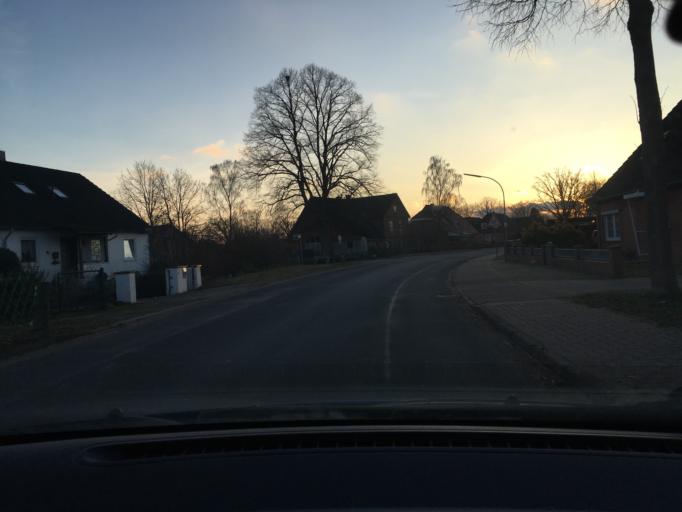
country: DE
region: Schleswig-Holstein
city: Brothen
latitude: 53.4808
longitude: 10.6677
